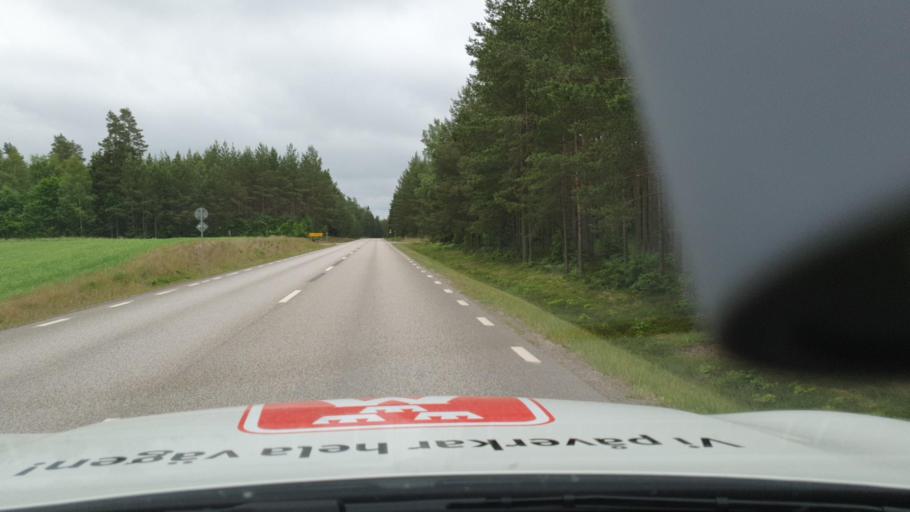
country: SE
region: Vaestra Goetaland
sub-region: Hjo Kommun
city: Hjo
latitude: 58.3473
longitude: 14.2234
